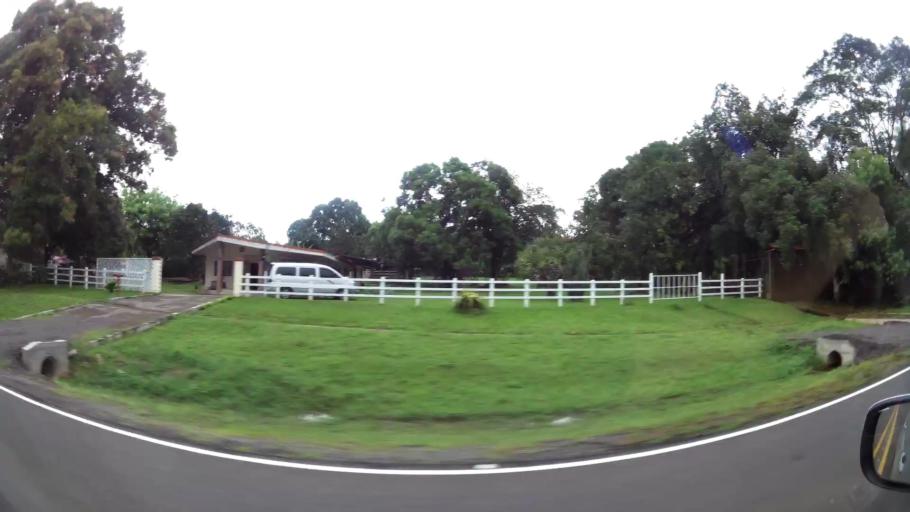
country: CR
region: Alajuela
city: Orotina
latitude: 9.9463
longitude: -84.5588
